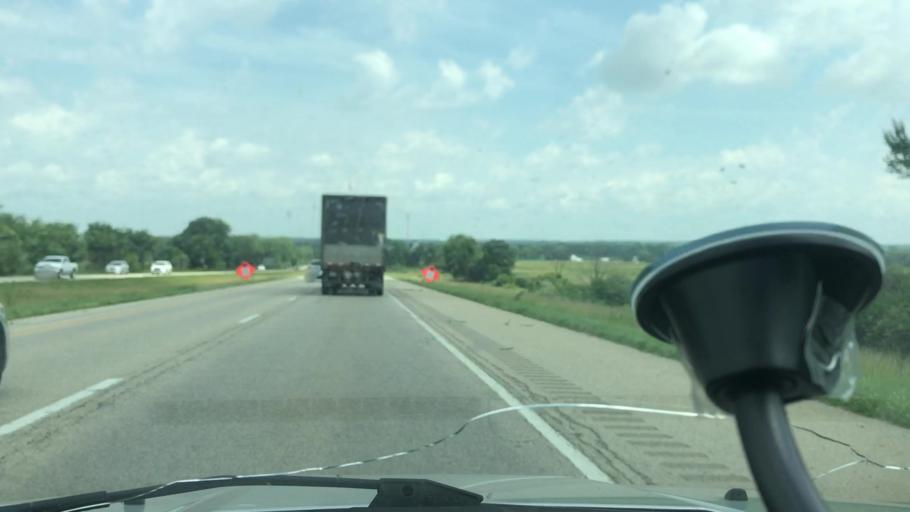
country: US
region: Illinois
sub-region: Peoria County
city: Bellevue
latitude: 40.7082
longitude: -89.6759
